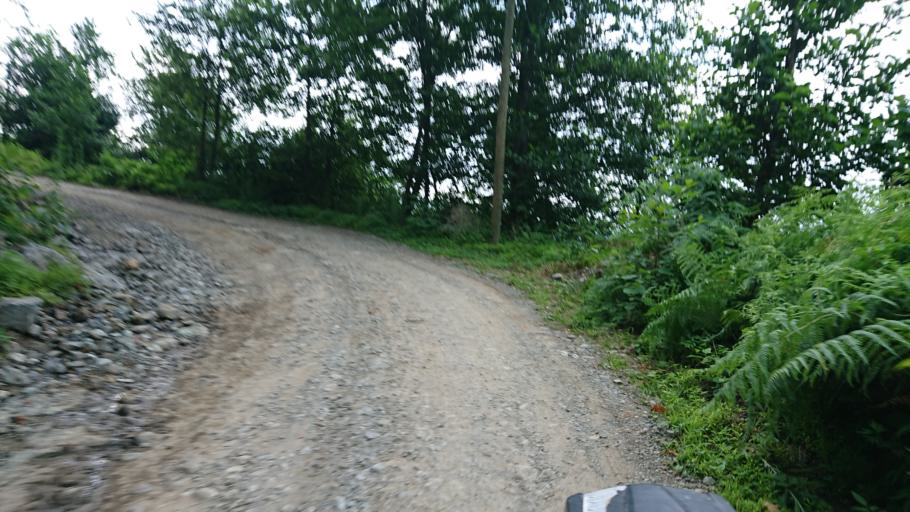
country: TR
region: Rize
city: Rize
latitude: 40.9888
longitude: 40.5151
